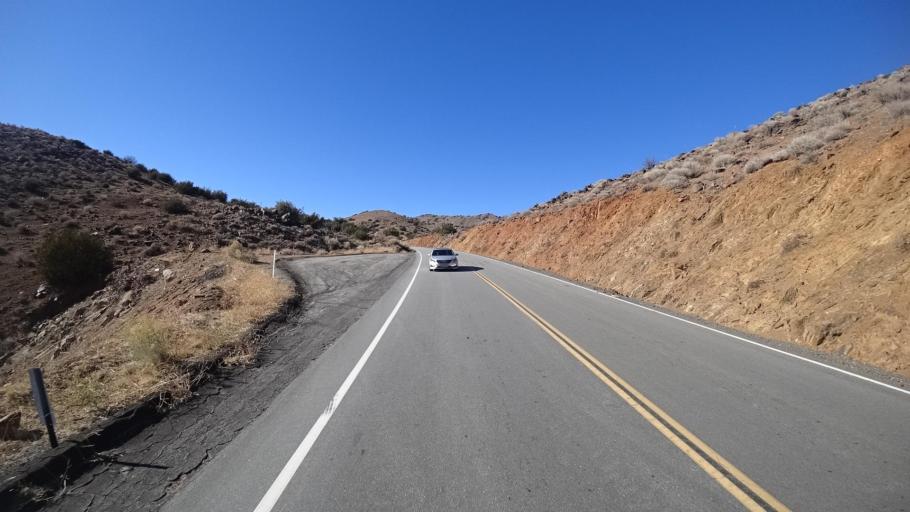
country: US
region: California
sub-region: Kern County
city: Wofford Heights
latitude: 35.6830
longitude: -118.3827
